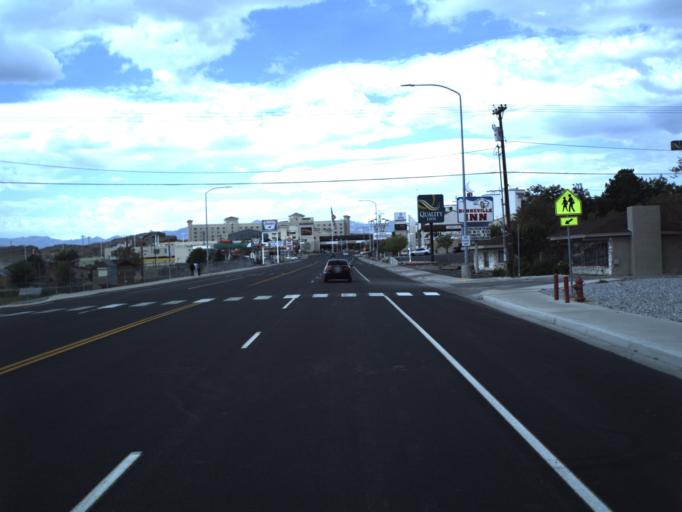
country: US
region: Utah
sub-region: Tooele County
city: Wendover
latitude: 40.7371
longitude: -114.0378
